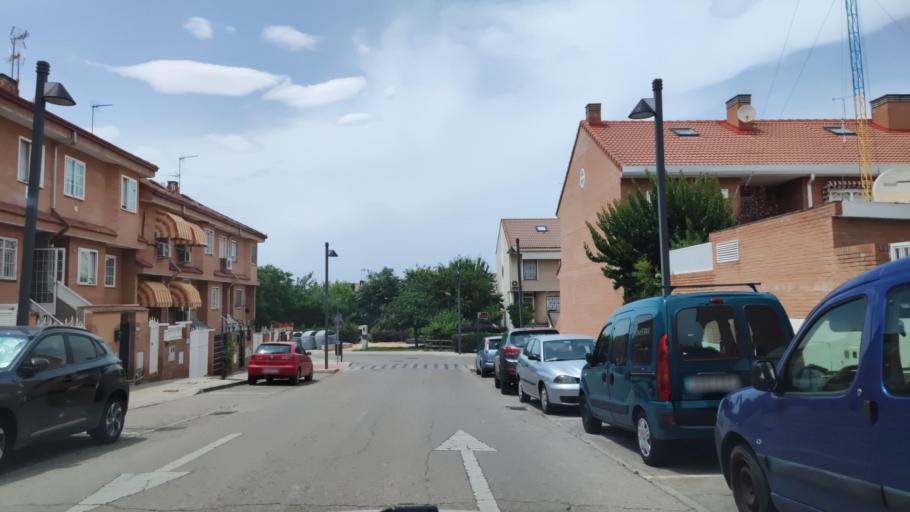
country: ES
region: Madrid
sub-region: Provincia de Madrid
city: Navalcarnero
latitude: 40.2859
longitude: -4.0222
